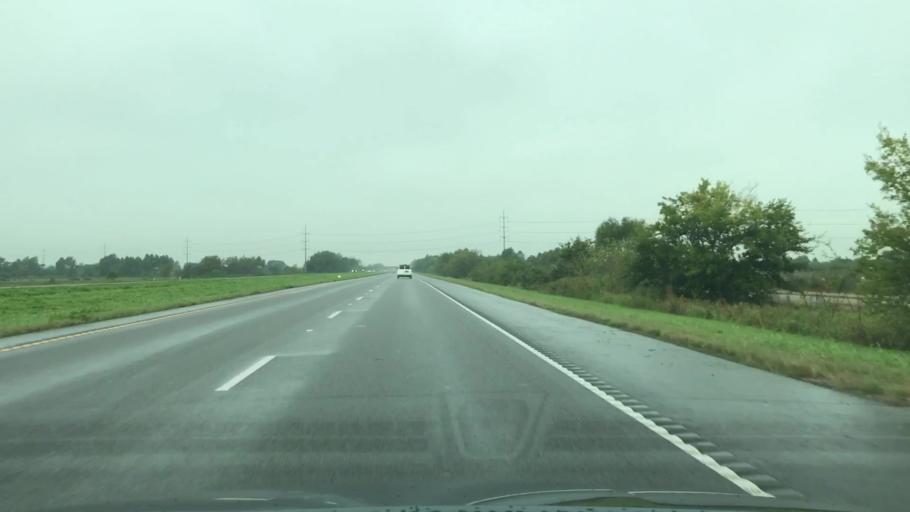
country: US
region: Louisiana
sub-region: Lafourche Parish
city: Raceland
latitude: 29.6901
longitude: -90.6078
